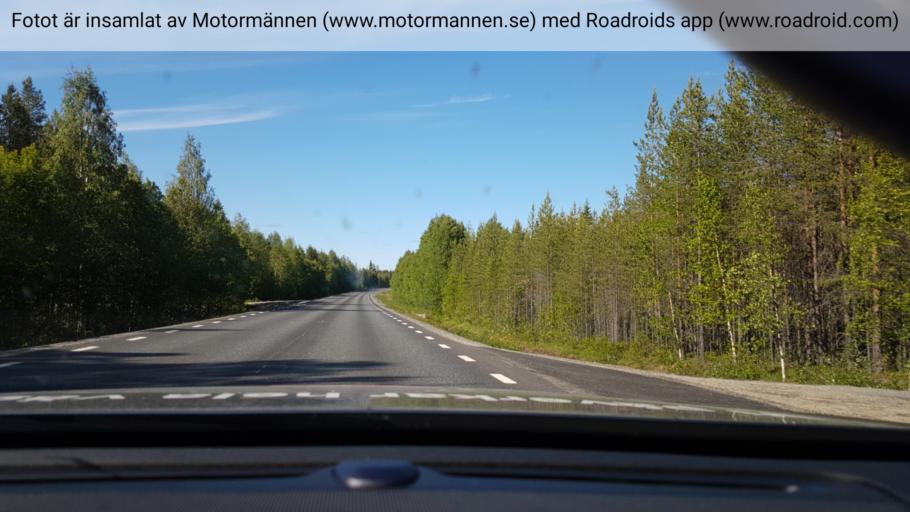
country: SE
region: Vaesterbotten
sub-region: Lycksele Kommun
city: Lycksele
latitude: 64.8001
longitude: 18.7318
